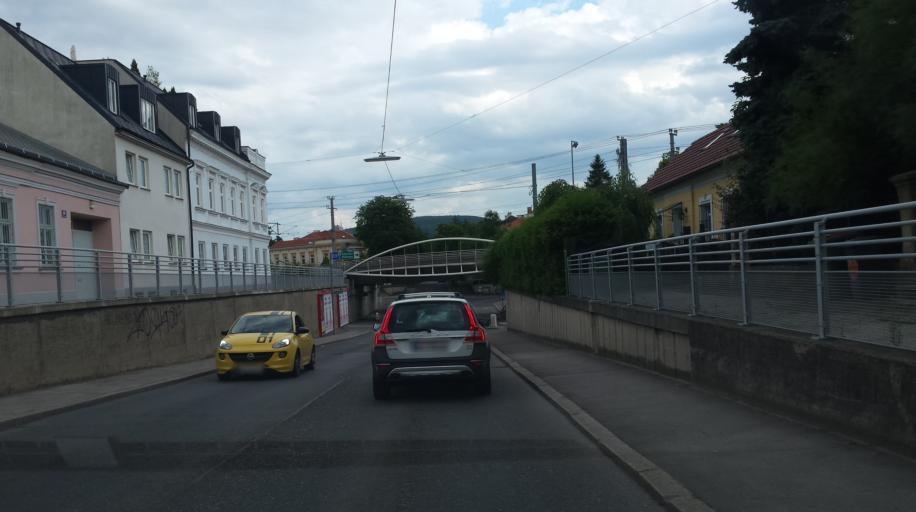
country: AT
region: Lower Austria
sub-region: Politischer Bezirk Wien-Umgebung
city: Purkersdorf
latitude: 48.2111
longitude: 16.2238
